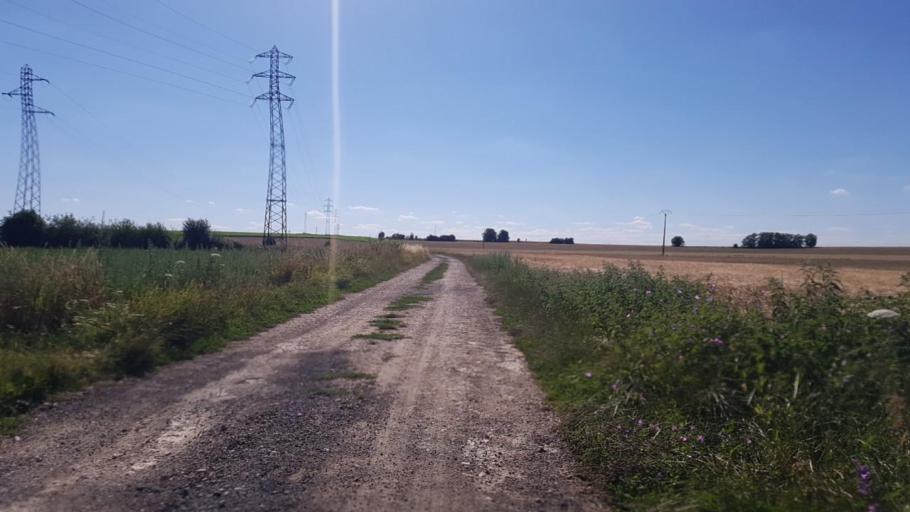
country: FR
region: Ile-de-France
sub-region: Departement de Seine-et-Marne
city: Chauconin-Neufmontiers
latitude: 48.9524
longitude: 2.8369
